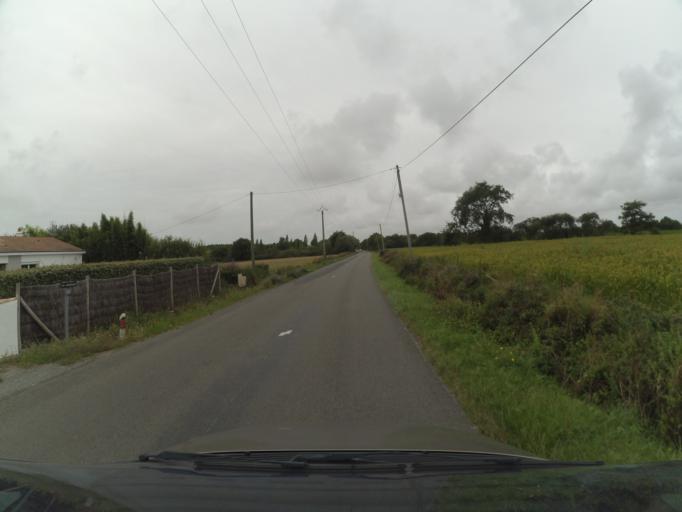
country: FR
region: Pays de la Loire
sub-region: Departement de la Vendee
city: Saint-Gervais
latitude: 46.8860
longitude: -1.9829
